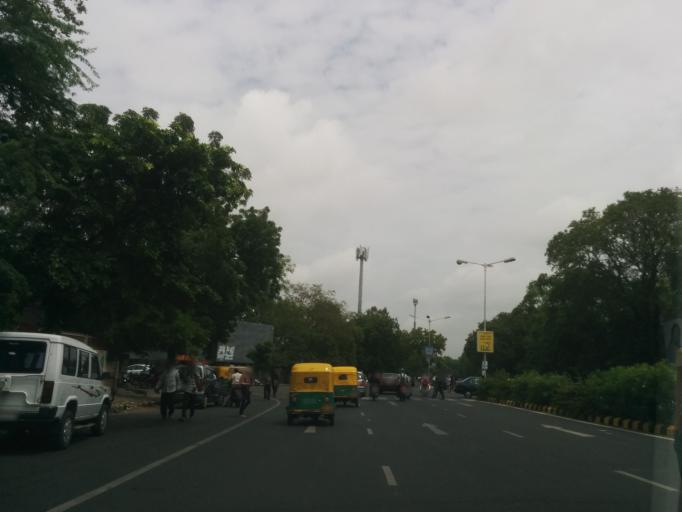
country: IN
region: Gujarat
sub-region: Ahmadabad
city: Ahmedabad
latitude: 23.0352
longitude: 72.5487
